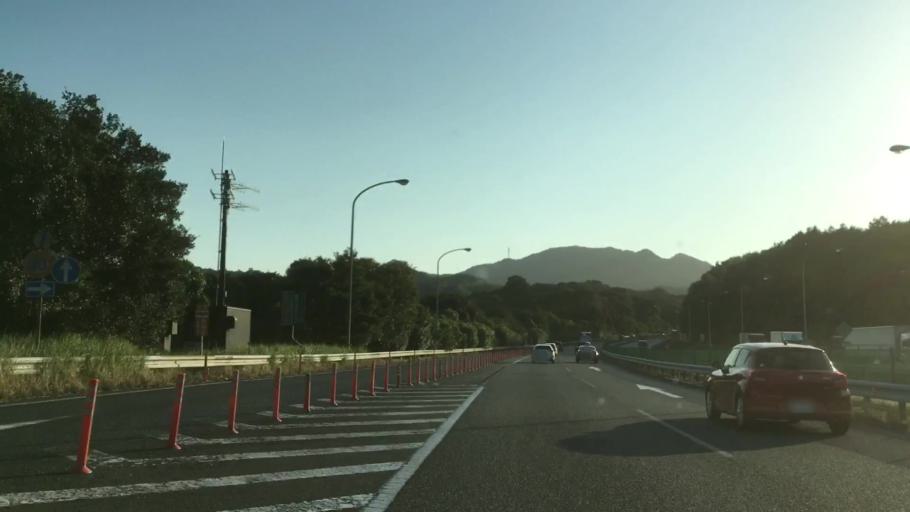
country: JP
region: Yamaguchi
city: Shimonoseki
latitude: 34.0501
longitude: 131.0041
